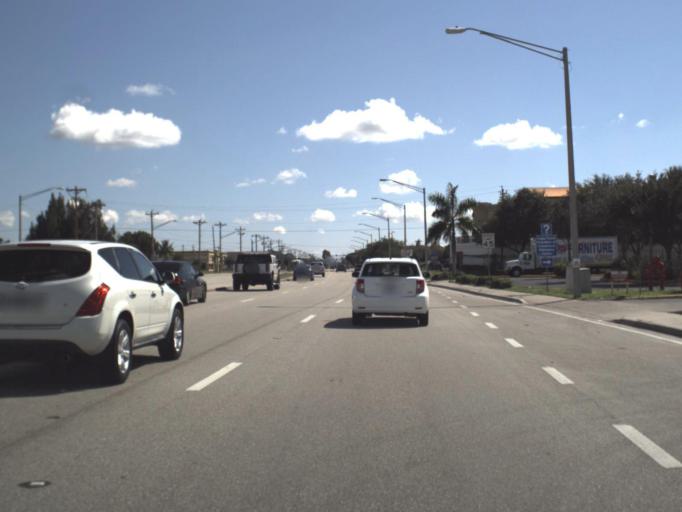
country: US
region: Florida
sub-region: Lee County
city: Lochmoor Waterway Estates
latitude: 26.6668
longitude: -81.9411
